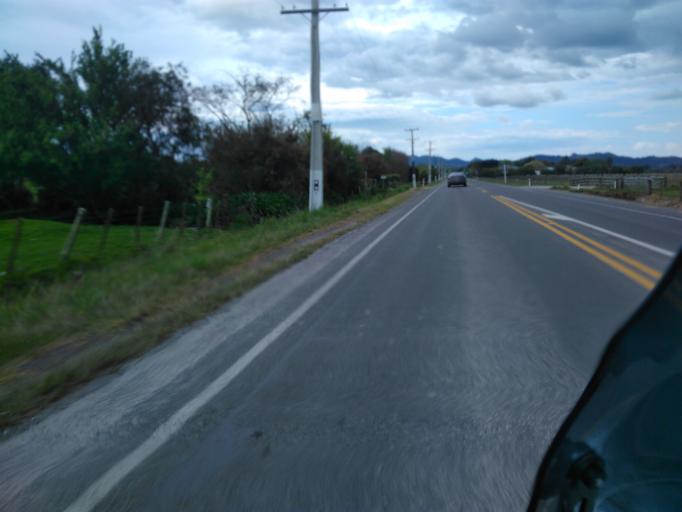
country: NZ
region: Gisborne
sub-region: Gisborne District
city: Gisborne
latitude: -38.6541
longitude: 177.9548
